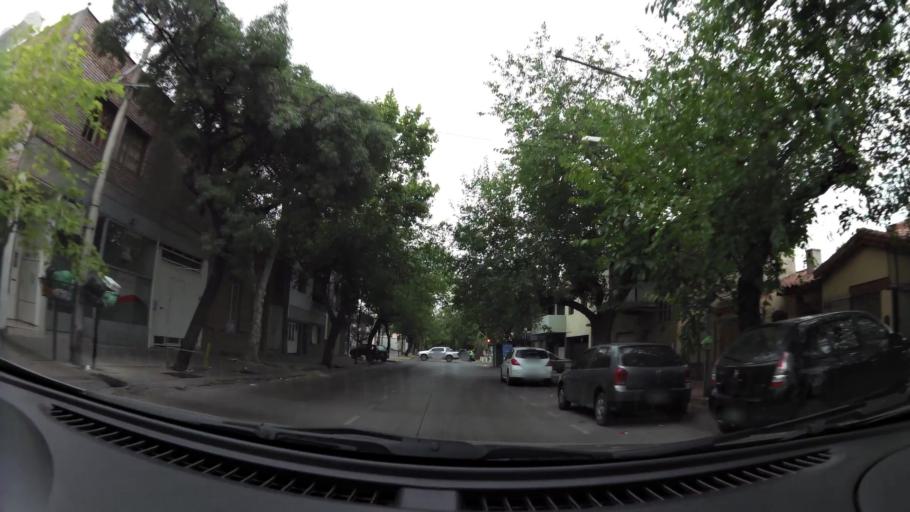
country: AR
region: Mendoza
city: Mendoza
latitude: -32.8816
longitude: -68.8581
